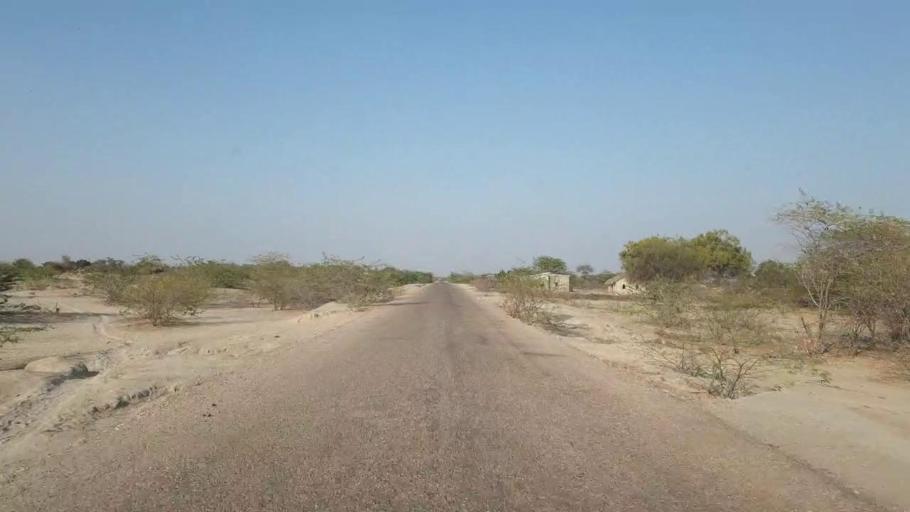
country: PK
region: Sindh
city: Chor
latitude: 25.5655
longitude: 69.8007
